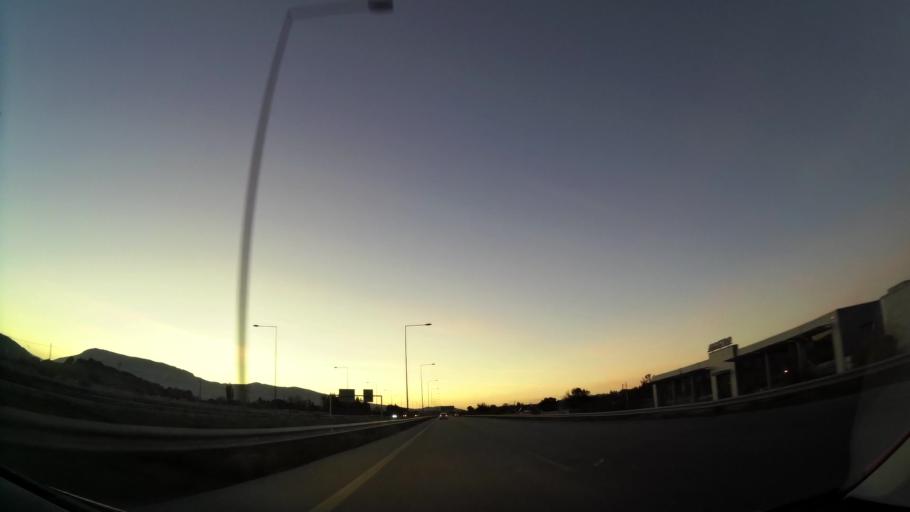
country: GR
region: Attica
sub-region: Nomarchia Anatolikis Attikis
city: Argithea
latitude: 37.9919
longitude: 23.9101
